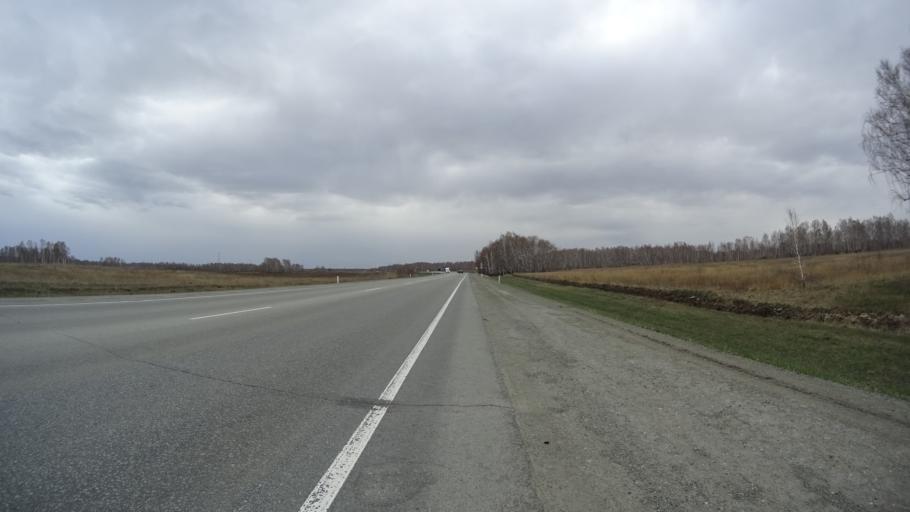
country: RU
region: Chelyabinsk
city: Yemanzhelinsk
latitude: 54.6995
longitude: 61.2518
